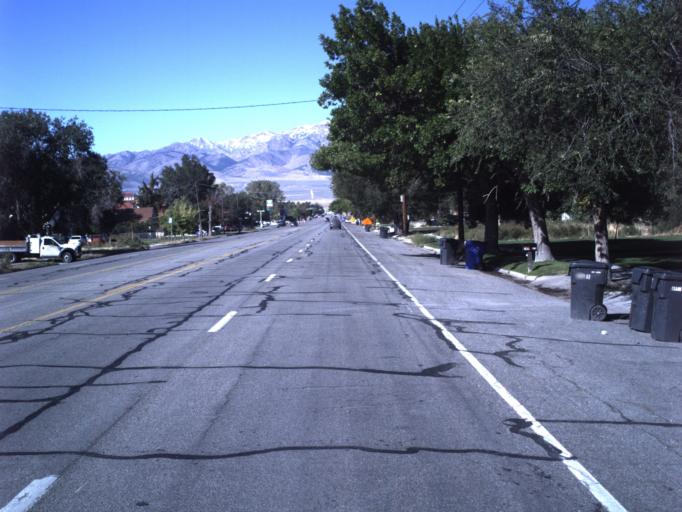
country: US
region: Utah
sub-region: Tooele County
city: Grantsville
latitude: 40.5999
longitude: -112.4593
